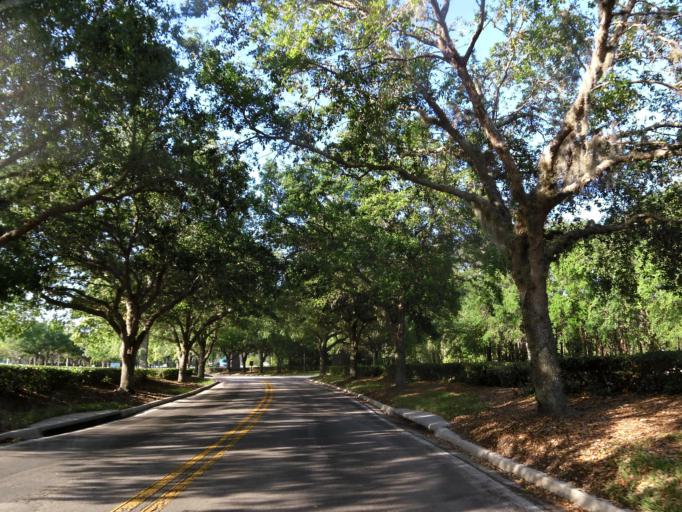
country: US
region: Florida
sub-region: Saint Johns County
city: Villano Beach
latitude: 29.9915
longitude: -81.4664
